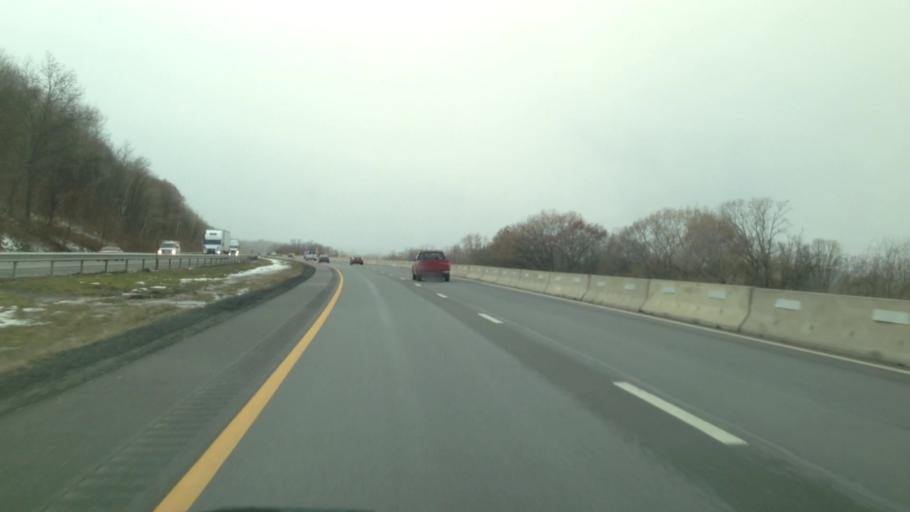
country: US
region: New York
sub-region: Schenectady County
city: Scotia
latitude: 42.8714
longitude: -74.0489
